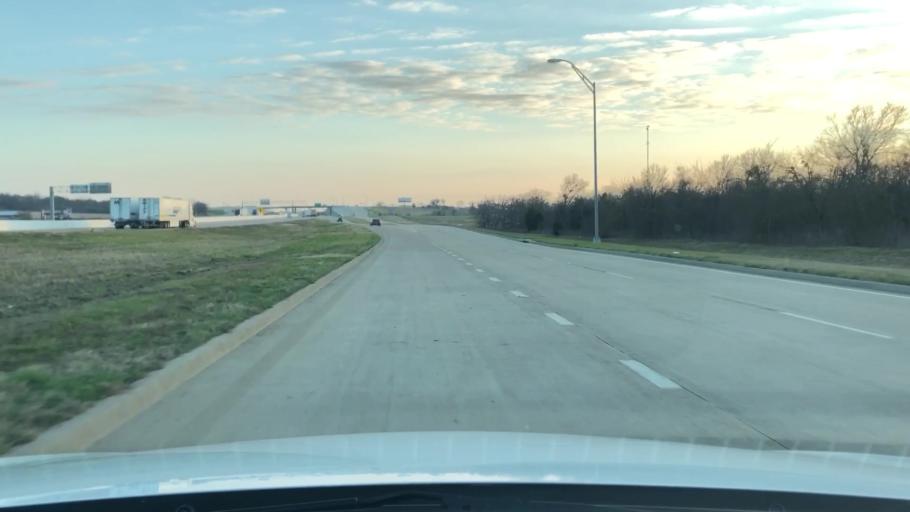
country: US
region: Texas
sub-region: McLennan County
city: West
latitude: 31.7951
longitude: -97.1030
